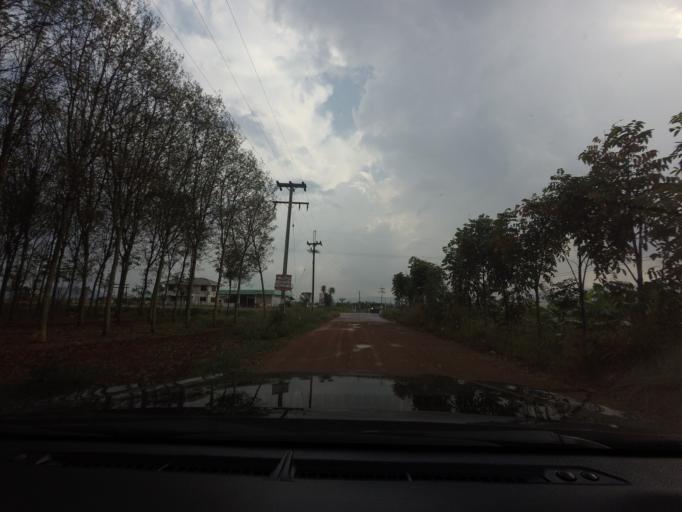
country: TH
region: Nakhon Ratchasima
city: Wang Nam Khiao
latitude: 14.4102
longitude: 101.7390
